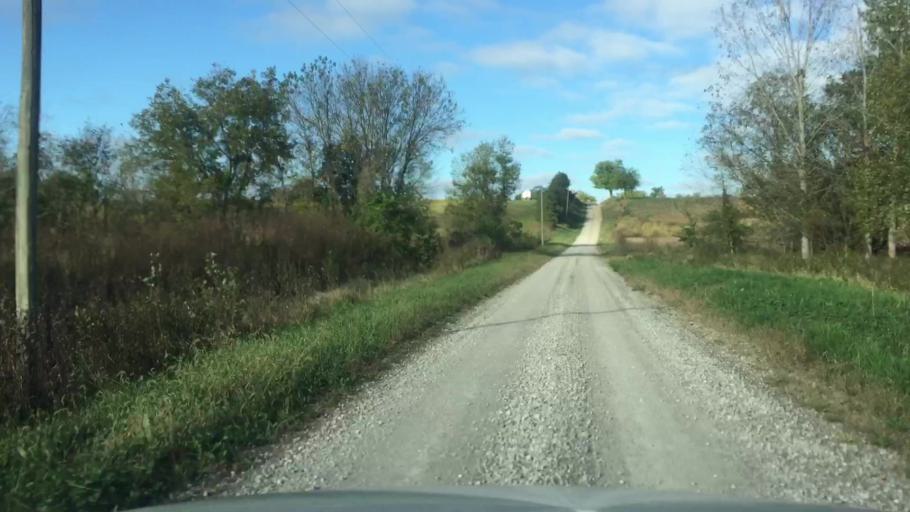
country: US
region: Missouri
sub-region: Howard County
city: New Franklin
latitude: 39.0833
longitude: -92.7701
